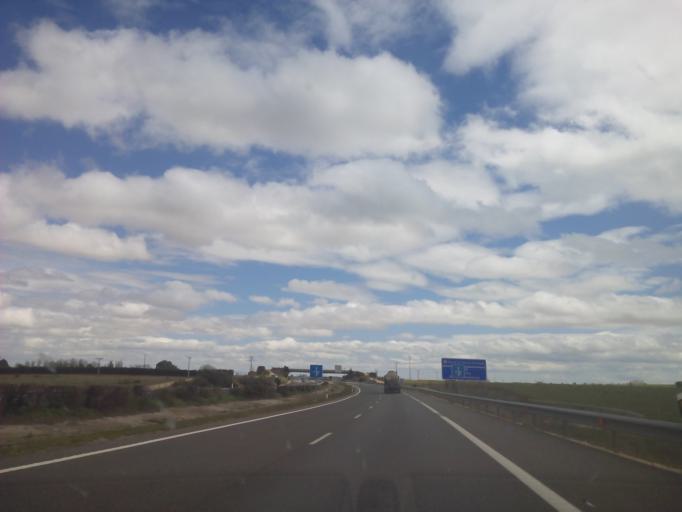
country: ES
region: Castille and Leon
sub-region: Provincia de Salamanca
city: Santa Marta de Tormes
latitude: 40.9442
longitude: -5.6134
